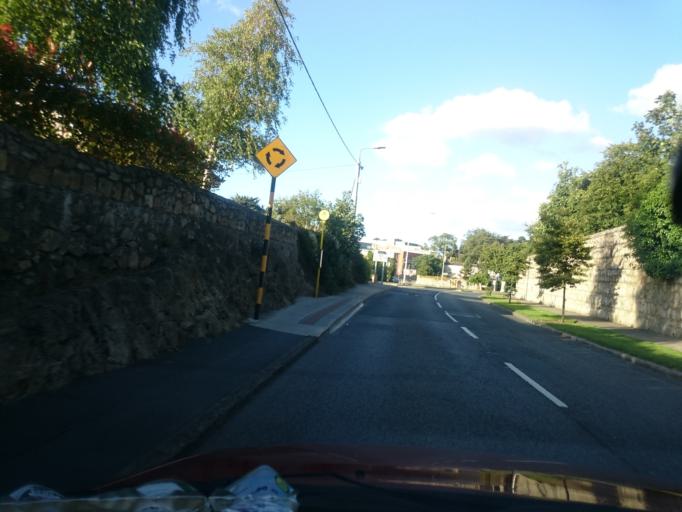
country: IE
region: Leinster
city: Ballinteer
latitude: 53.2781
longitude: -6.2463
